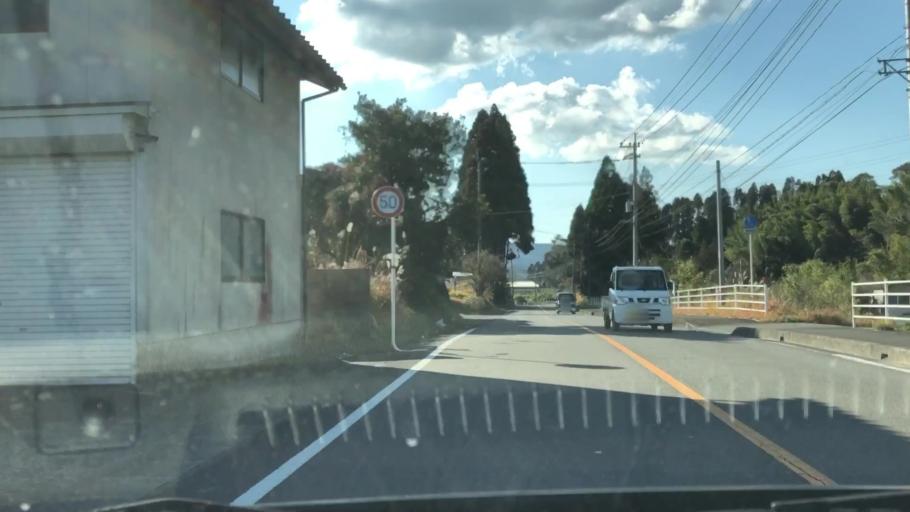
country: JP
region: Kagoshima
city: Satsumasendai
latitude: 31.8568
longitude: 130.3769
